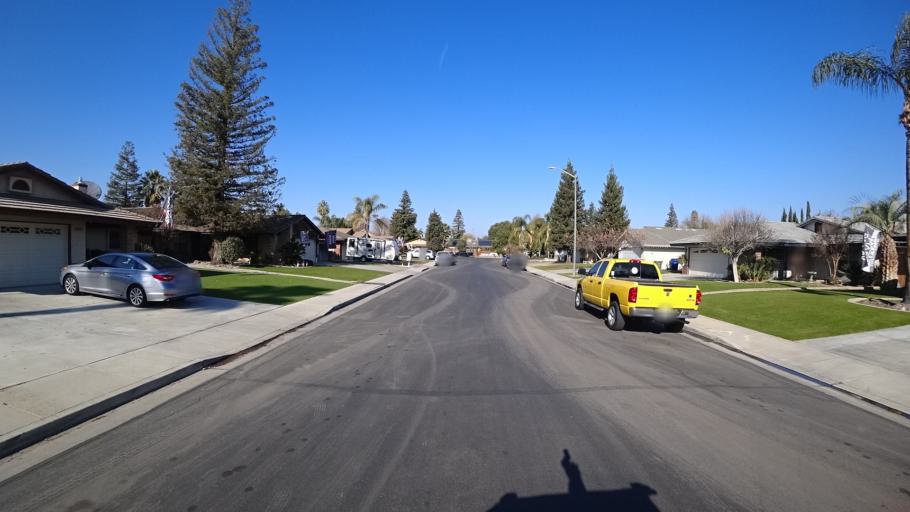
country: US
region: California
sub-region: Kern County
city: Greenacres
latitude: 35.3218
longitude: -119.1231
